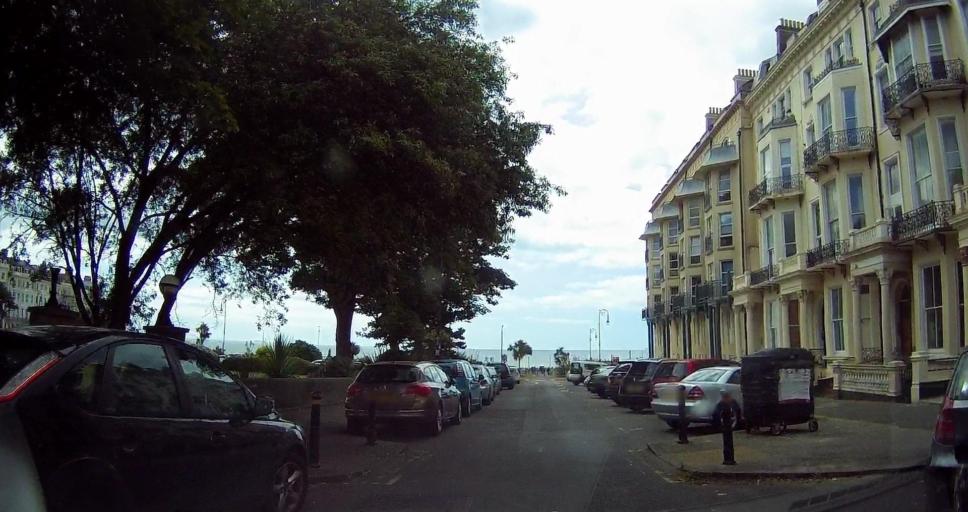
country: GB
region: England
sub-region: East Sussex
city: Hastings
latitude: 50.8533
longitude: 0.5621
